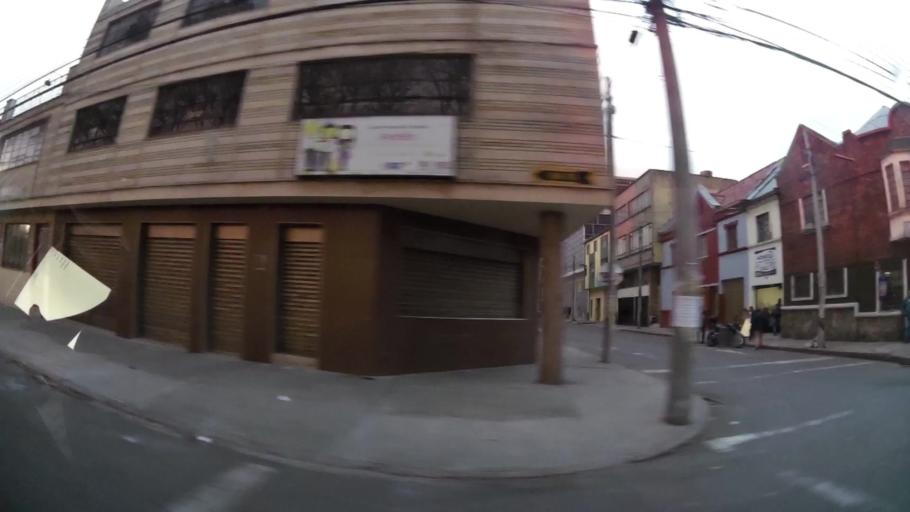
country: CO
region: Bogota D.C.
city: Bogota
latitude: 4.6083
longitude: -74.0904
